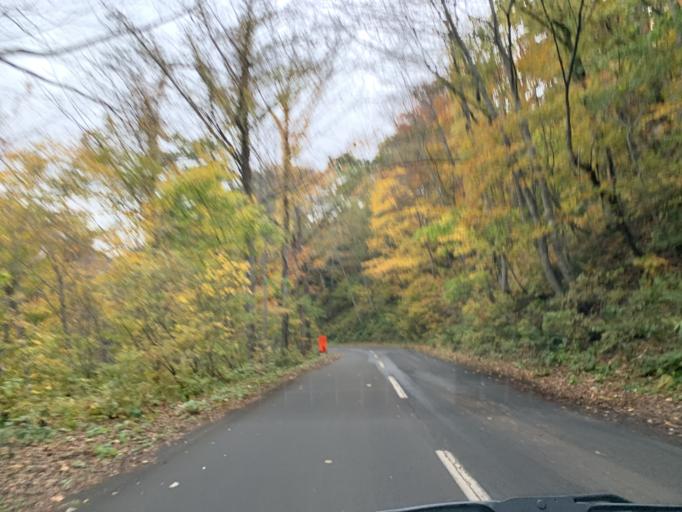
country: JP
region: Iwate
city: Mizusawa
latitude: 39.1072
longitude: 140.8607
